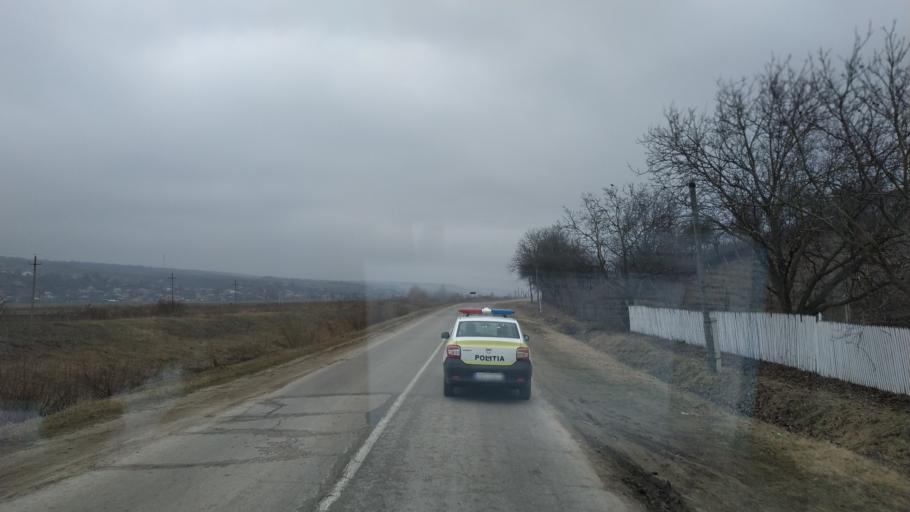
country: MD
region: Hincesti
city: Hincesti
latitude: 46.9759
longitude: 28.4696
